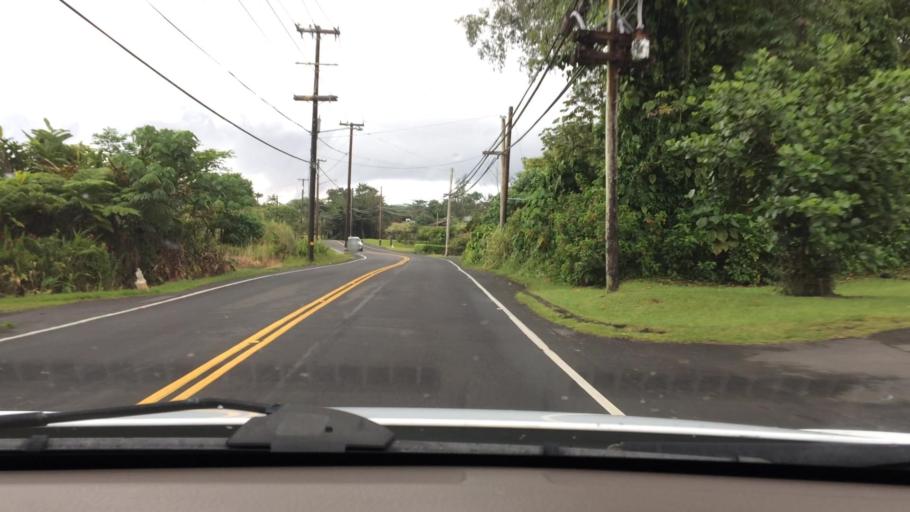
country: US
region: Hawaii
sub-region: Hawaii County
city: Hawaiian Paradise Park
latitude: 19.4983
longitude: -154.9530
